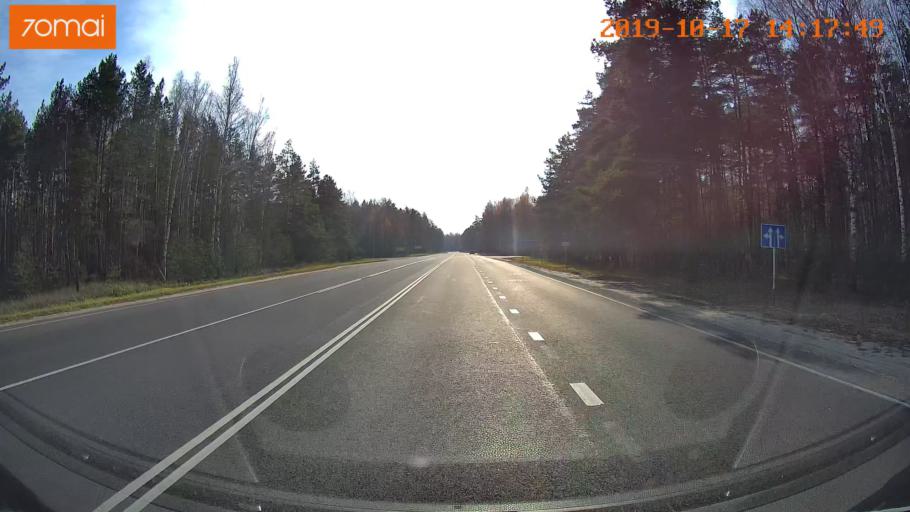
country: RU
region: Rjazan
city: Spas-Klepiki
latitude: 55.0709
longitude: 40.0362
